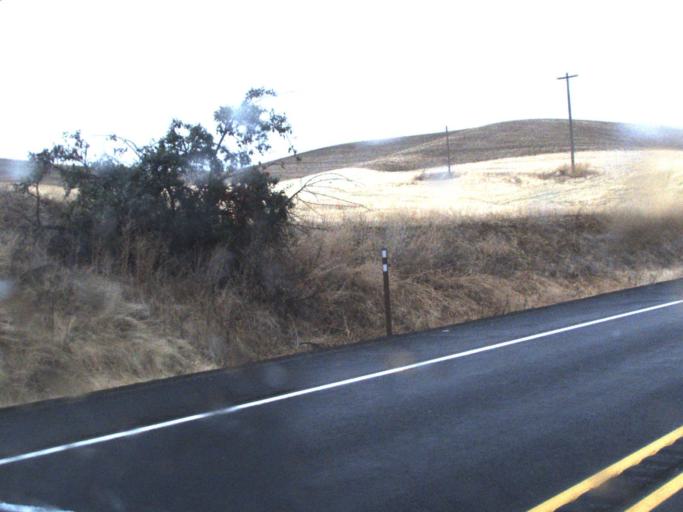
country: US
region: Washington
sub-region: Whitman County
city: Colfax
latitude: 46.9110
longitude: -117.3511
